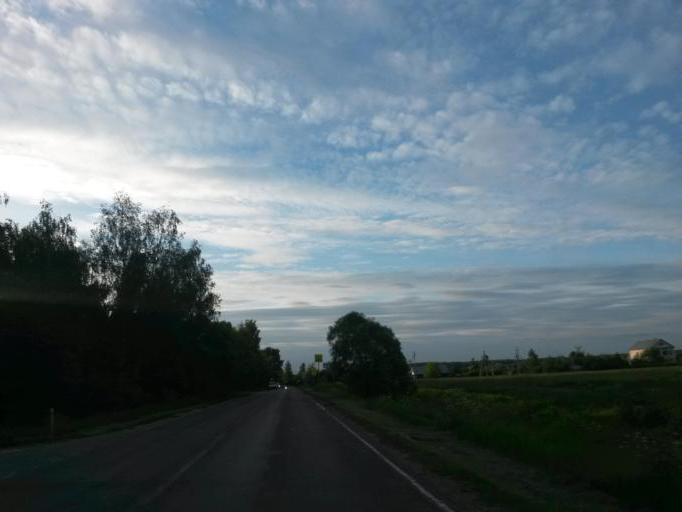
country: RU
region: Moskovskaya
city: Lyubuchany
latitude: 55.2445
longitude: 37.6406
